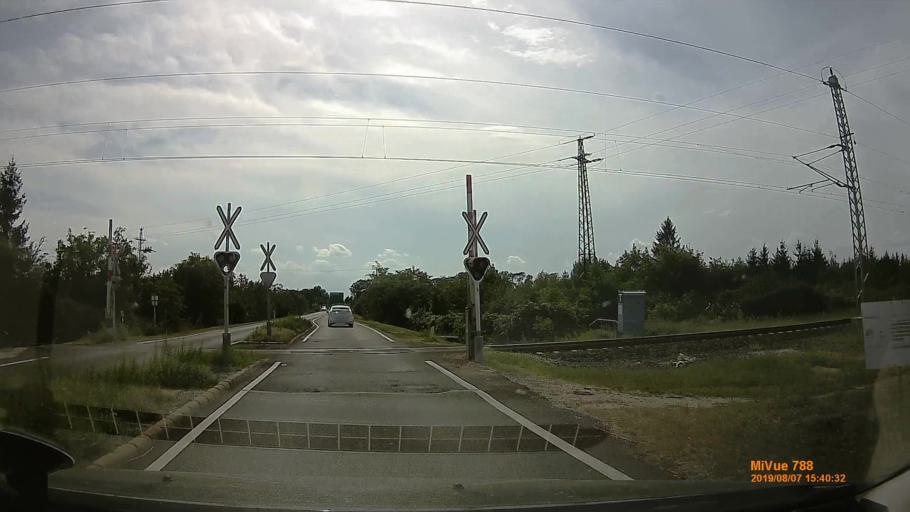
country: HU
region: Vas
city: Szombathely
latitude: 47.2135
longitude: 16.6475
